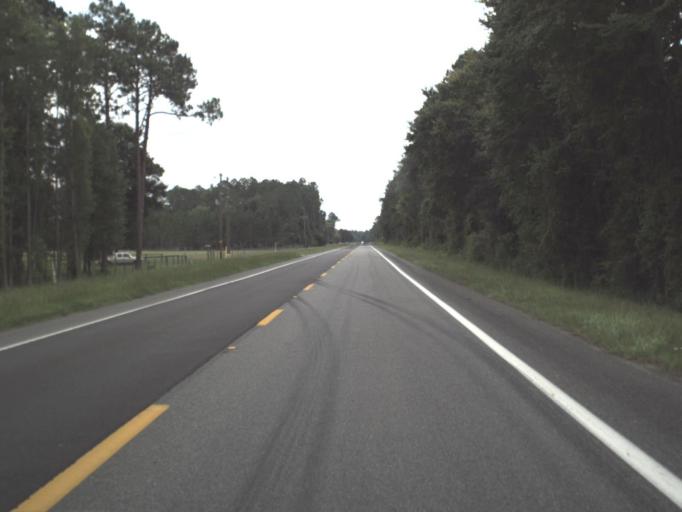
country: US
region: Florida
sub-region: Union County
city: Lake Butler
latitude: 30.0365
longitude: -82.3759
